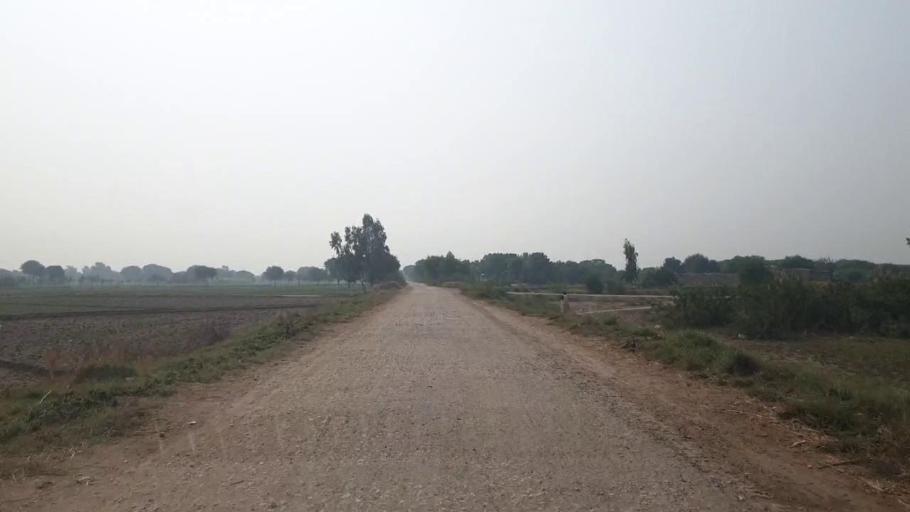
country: PK
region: Sindh
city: Tando Muhammad Khan
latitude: 25.2416
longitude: 68.5712
